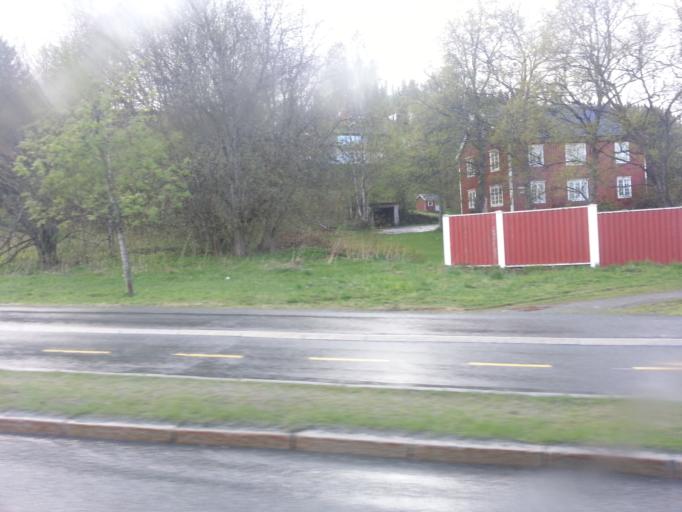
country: NO
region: Sor-Trondelag
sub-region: Trondheim
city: Trondheim
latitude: 63.4033
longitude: 10.3582
